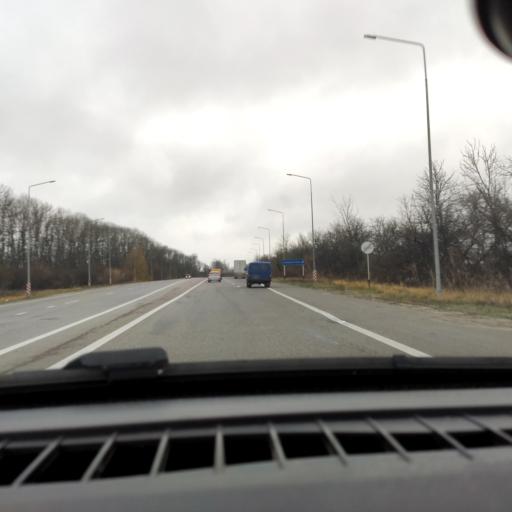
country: RU
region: Voronezj
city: Kolodeznyy
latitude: 51.3350
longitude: 39.0248
